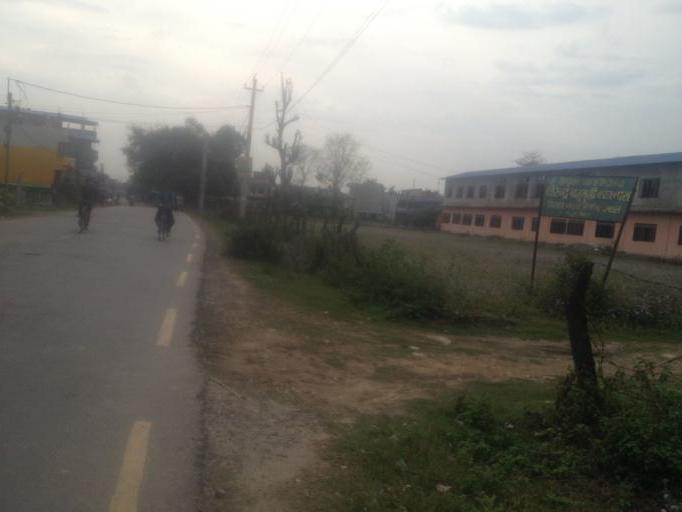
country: NP
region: Central Region
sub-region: Narayani Zone
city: Bharatpur
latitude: 27.6919
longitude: 84.4383
